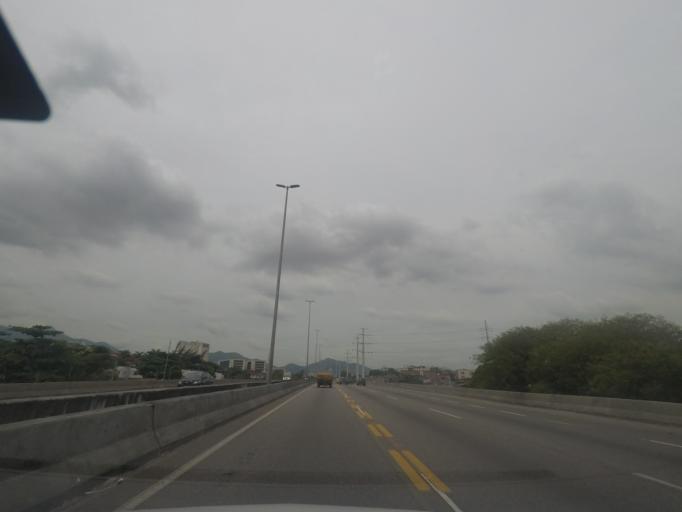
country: BR
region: Rio de Janeiro
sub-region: Rio De Janeiro
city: Rio de Janeiro
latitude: -22.8726
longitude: -43.2668
